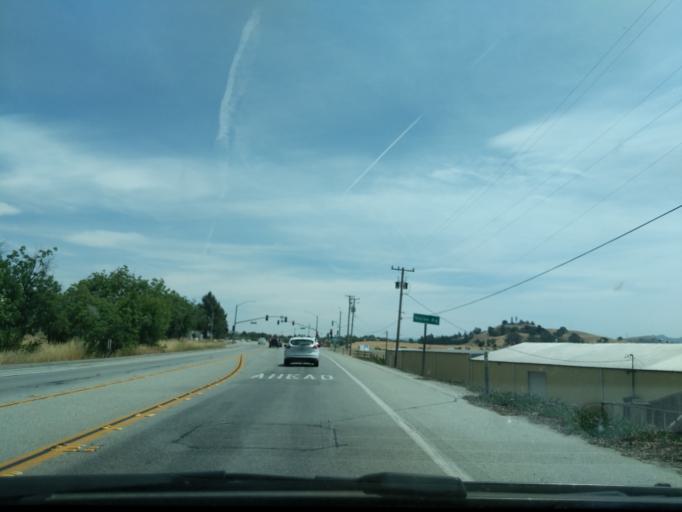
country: US
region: California
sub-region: San Benito County
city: Ridgemark
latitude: 36.8280
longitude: -121.3834
